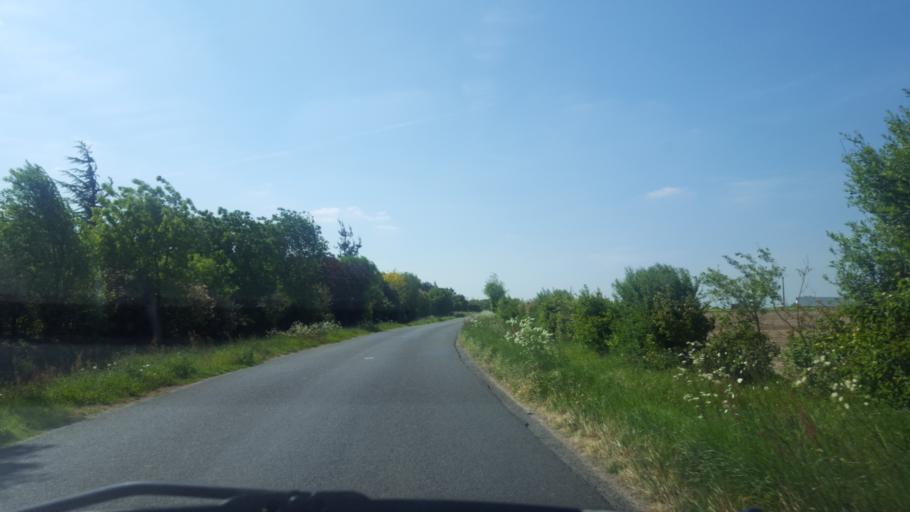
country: FR
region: Pays de la Loire
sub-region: Departement de la Loire-Atlantique
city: La Limouziniere
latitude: 47.0368
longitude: -1.5924
